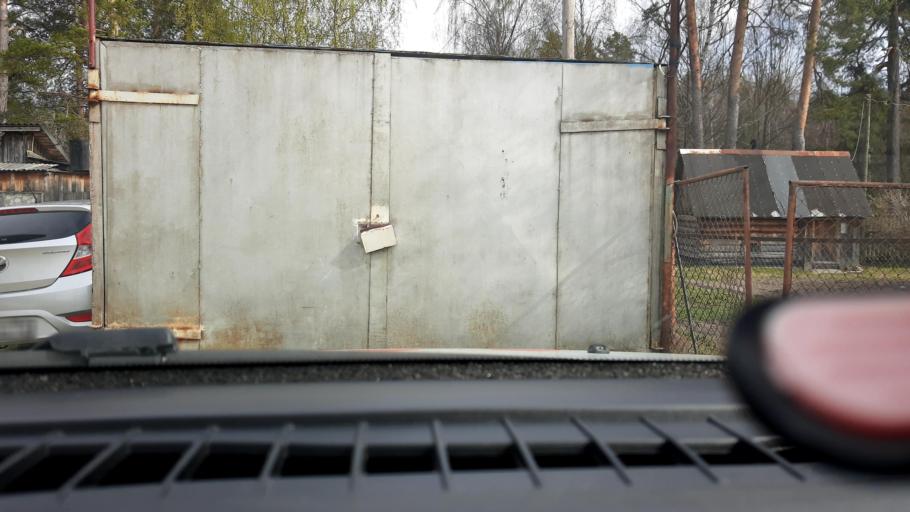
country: RU
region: Nizjnij Novgorod
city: Krasnyye Baki
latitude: 57.1638
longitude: 45.1972
